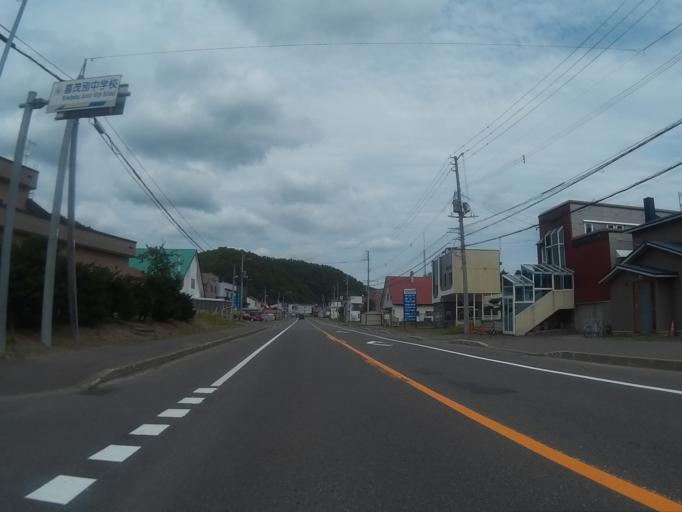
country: JP
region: Hokkaido
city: Niseko Town
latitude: 42.7956
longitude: 140.9387
